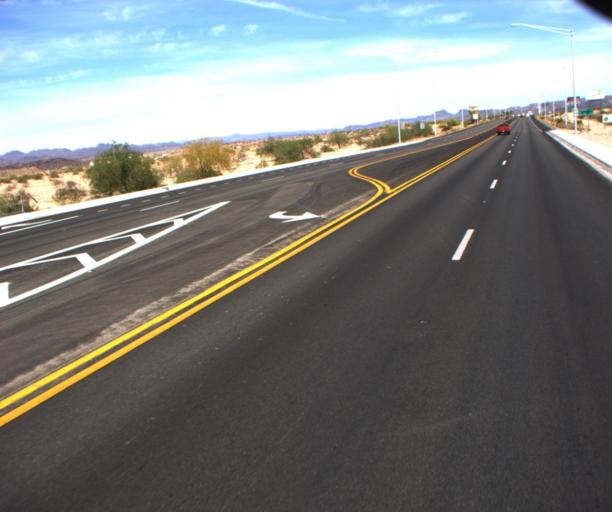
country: US
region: Arizona
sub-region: La Paz County
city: Parker
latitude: 34.1563
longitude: -114.2752
